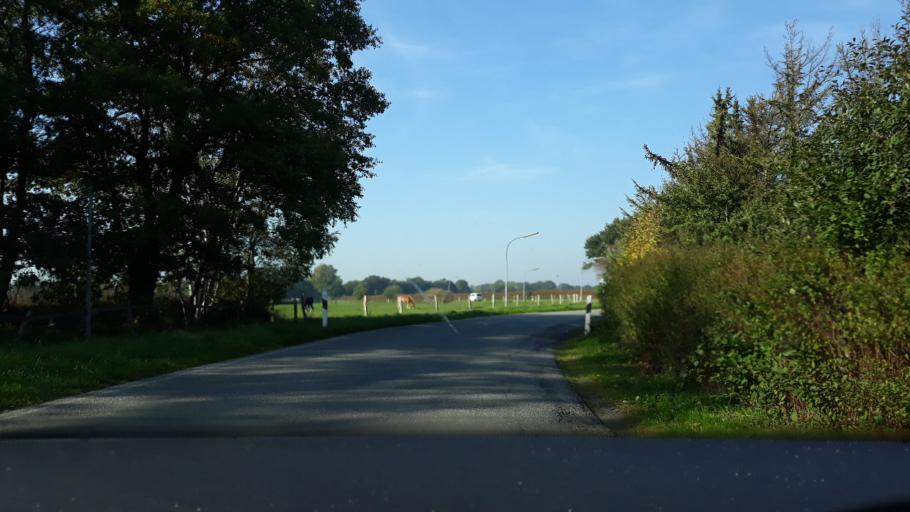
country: DE
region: Schleswig-Holstein
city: Klein Bennebek
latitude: 54.4019
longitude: 9.4398
